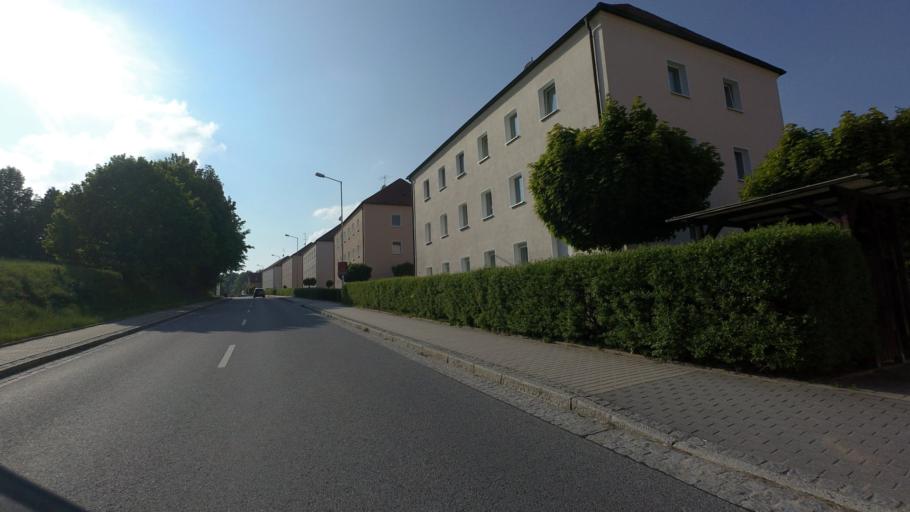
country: DE
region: Saxony
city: Sebnitz
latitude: 50.9832
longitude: 14.2698
